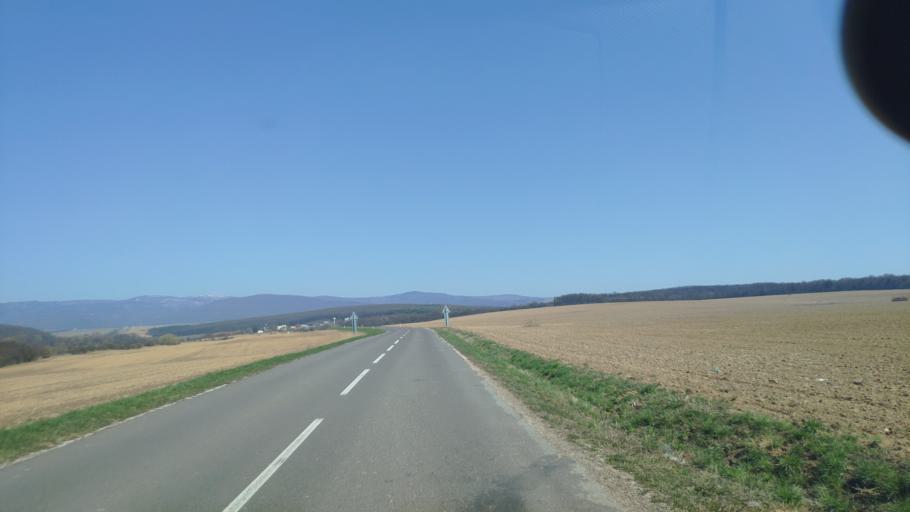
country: SK
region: Kosicky
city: Moldava nad Bodvou
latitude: 48.6338
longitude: 21.0092
